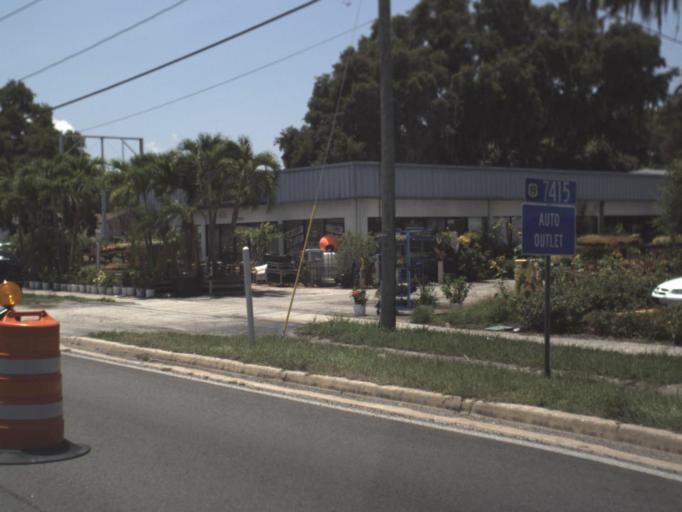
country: US
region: Florida
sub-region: Pasco County
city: Port Richey
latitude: 28.2645
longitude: -82.7279
